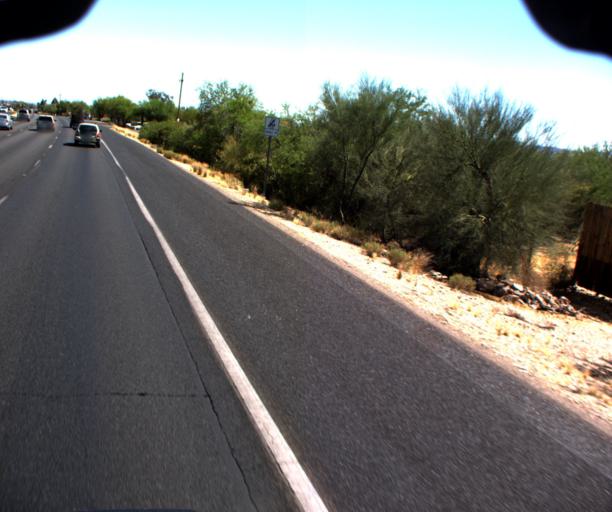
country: US
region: Arizona
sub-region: Pima County
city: Casas Adobes
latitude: 32.3333
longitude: -110.9774
